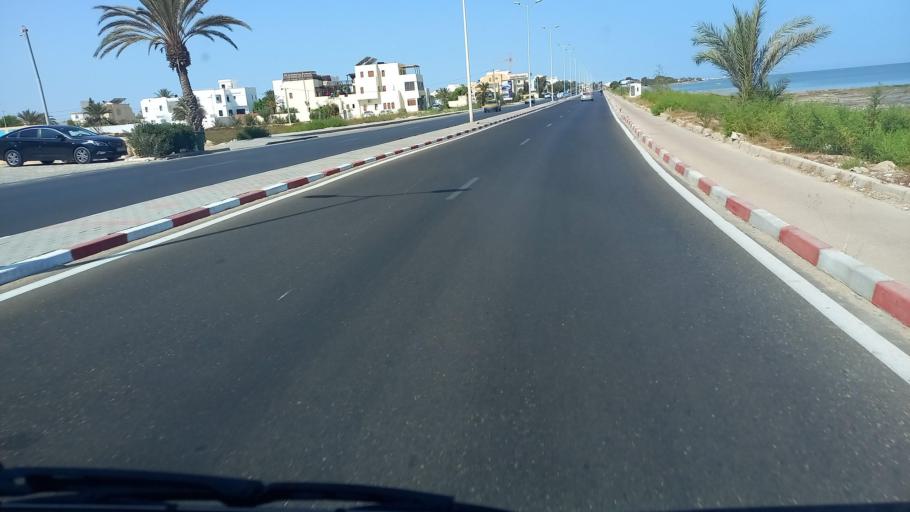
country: TN
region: Madanin
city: Houmt Souk
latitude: 33.8739
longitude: 10.8979
